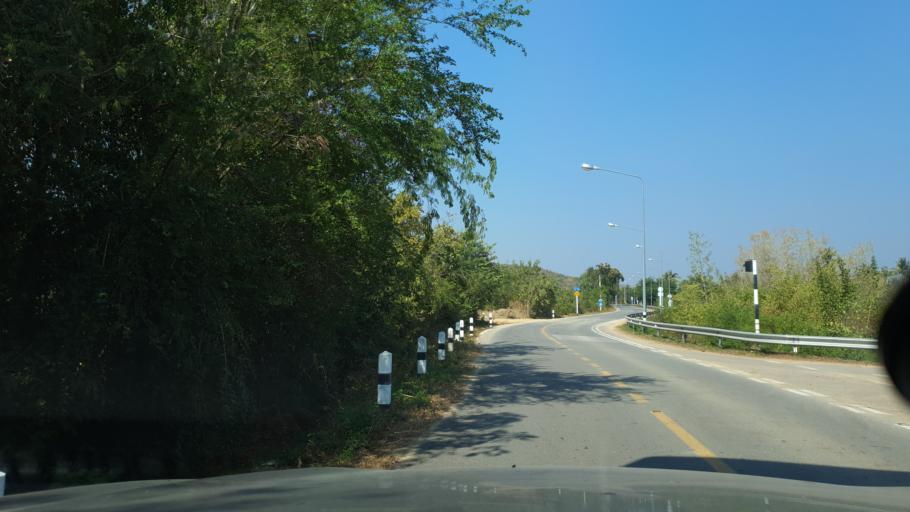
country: TH
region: Prachuap Khiri Khan
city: Sam Roi Yot
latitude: 12.2809
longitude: 99.9730
